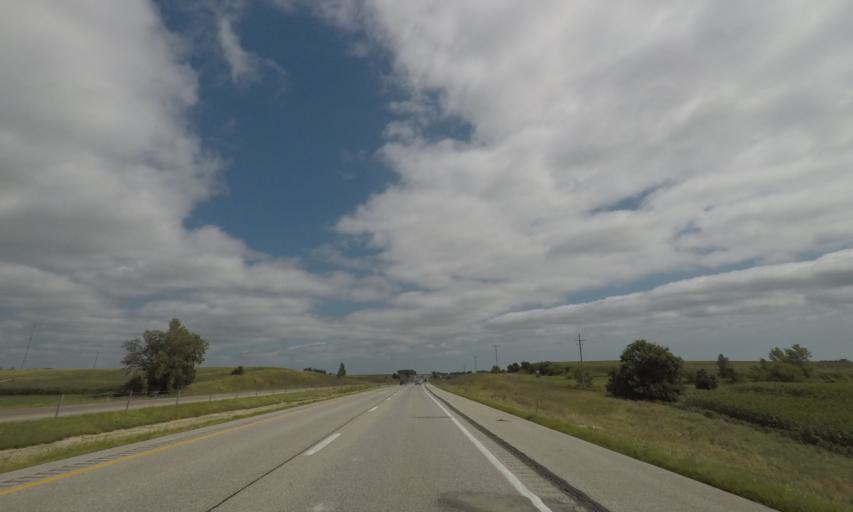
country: US
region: Iowa
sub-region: Iowa County
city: Marengo
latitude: 41.6961
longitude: -92.1844
